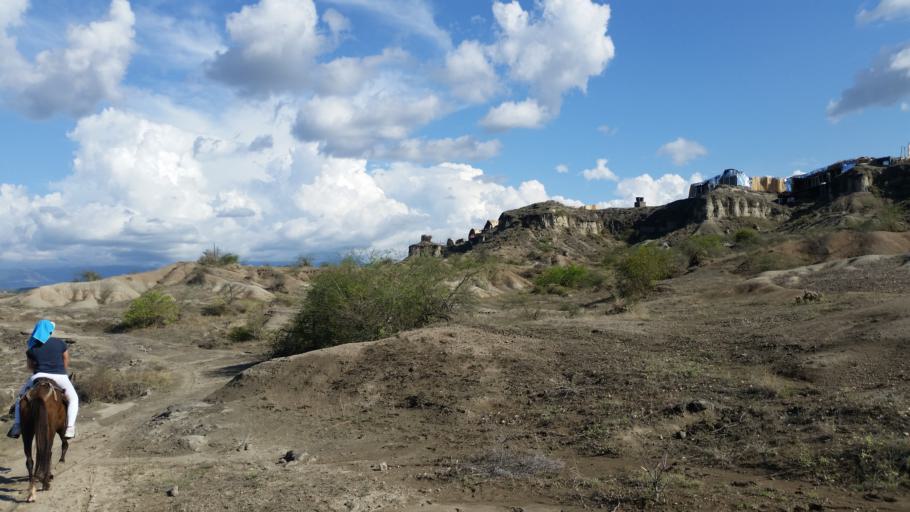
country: CO
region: Huila
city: Villavieja
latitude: 3.2545
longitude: -75.1343
